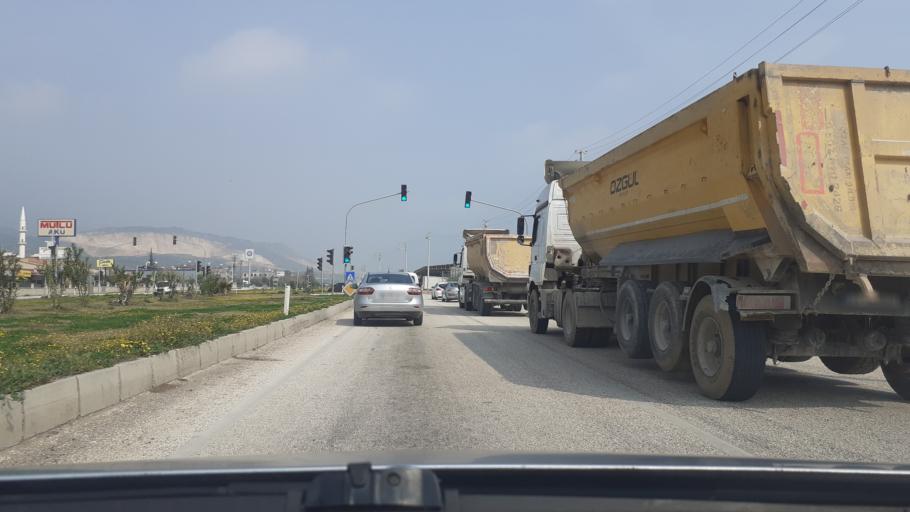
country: TR
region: Hatay
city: Kirikhan
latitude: 36.5229
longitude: 36.3772
